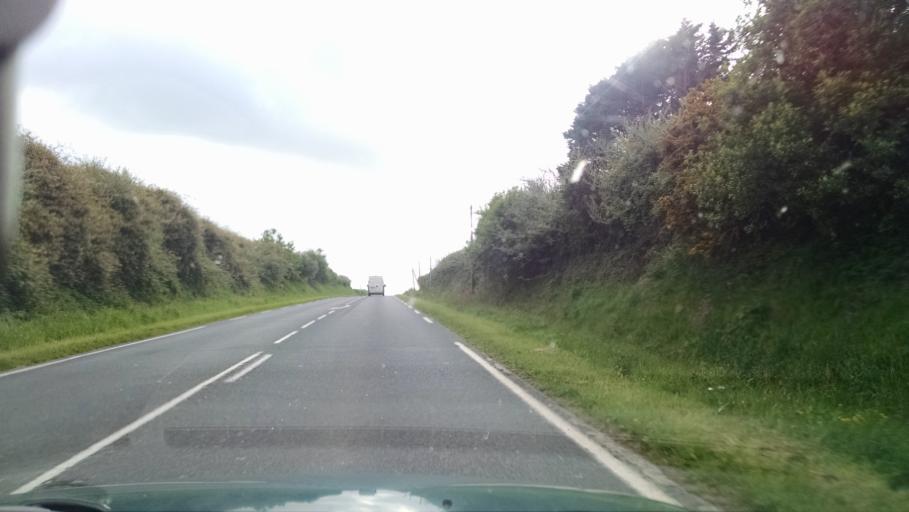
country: FR
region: Brittany
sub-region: Departement du Finistere
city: Saint-Pol-de-Leon
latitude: 48.6640
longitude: -3.9808
